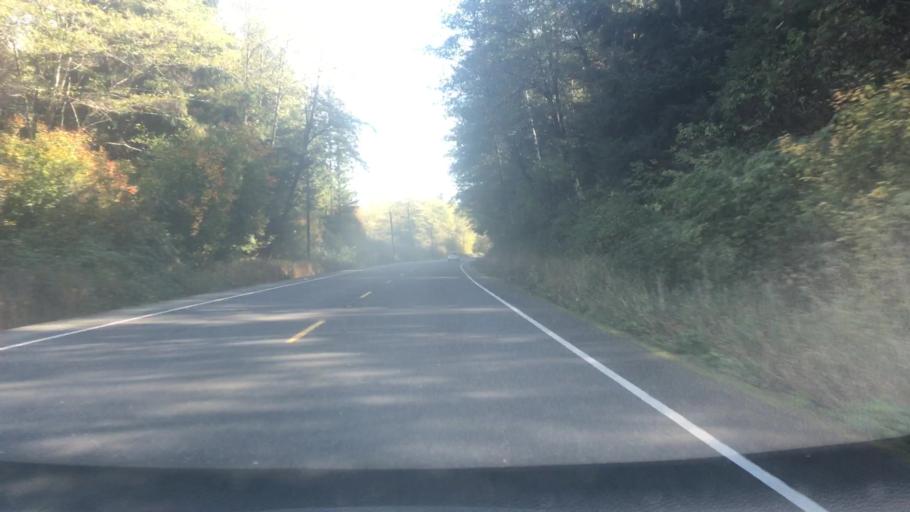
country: US
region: Oregon
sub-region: Lincoln County
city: Rose Lodge
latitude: 45.0113
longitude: -123.9251
